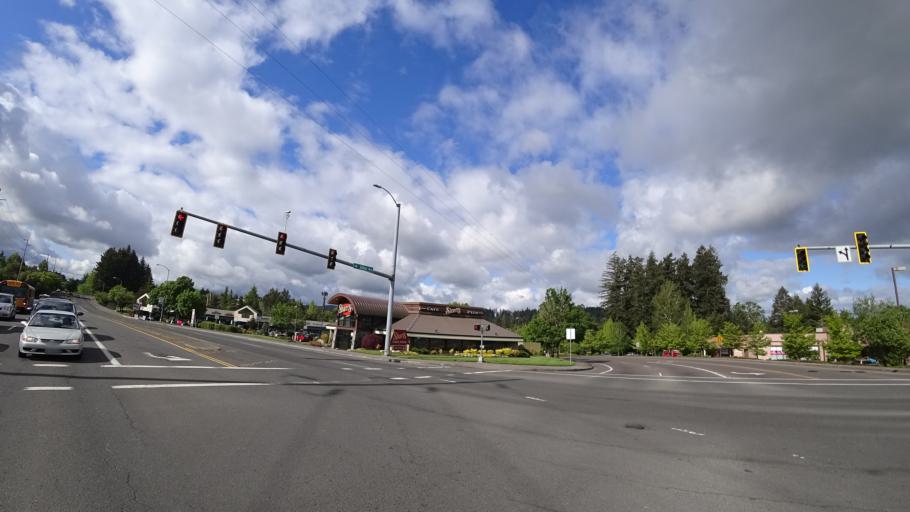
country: US
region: Oregon
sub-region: Washington County
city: Beaverton
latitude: 45.4764
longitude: -122.8260
